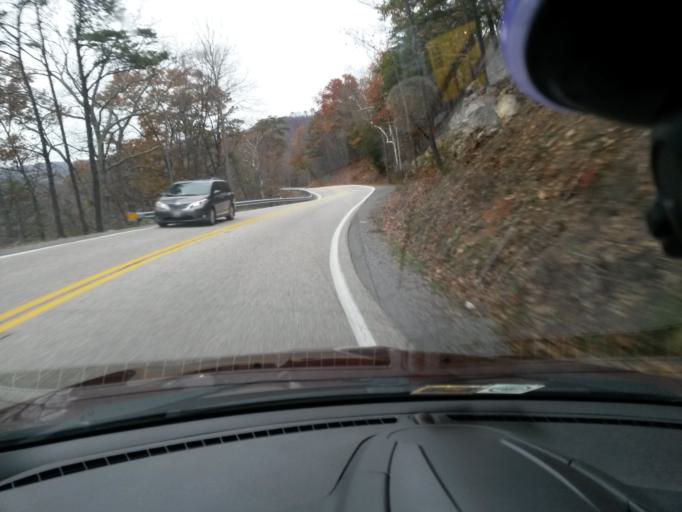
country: US
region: Virginia
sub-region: Rockbridge County
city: Glasgow
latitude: 37.6136
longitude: -79.4322
